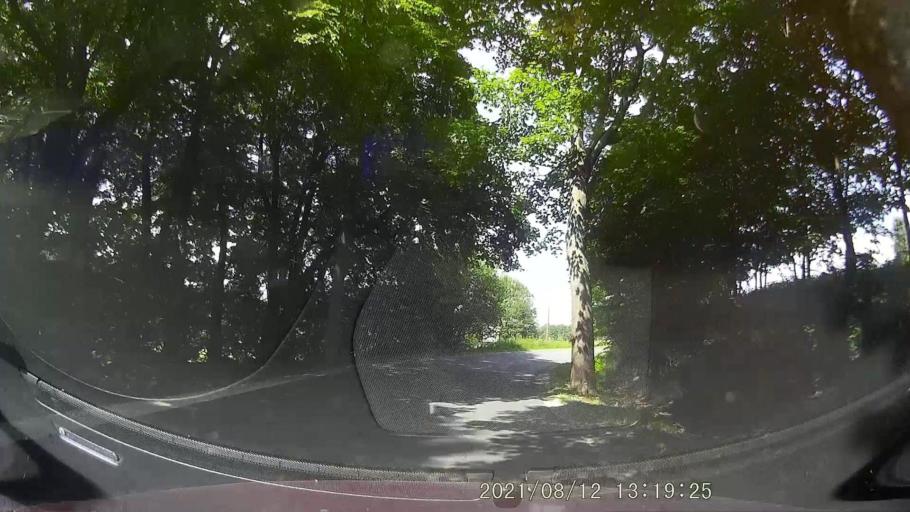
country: PL
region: Lower Silesian Voivodeship
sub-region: Powiat klodzki
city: Stronie Slaskie
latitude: 50.2790
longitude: 16.8827
